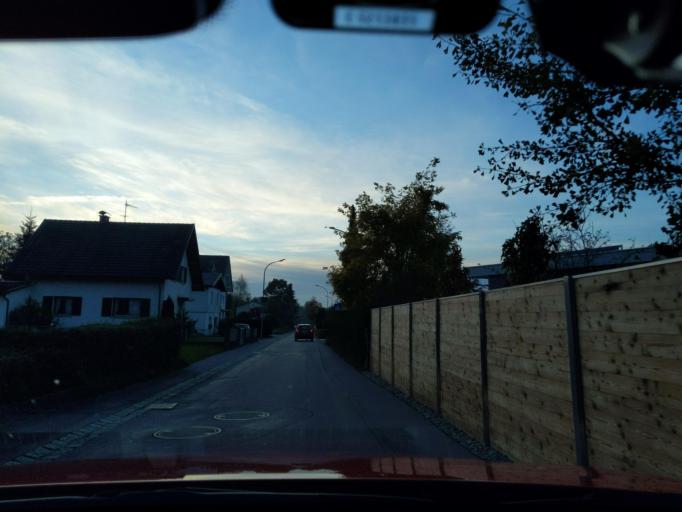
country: AT
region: Vorarlberg
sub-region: Politischer Bezirk Bregenz
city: Lochau
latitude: 47.5367
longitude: 9.7430
